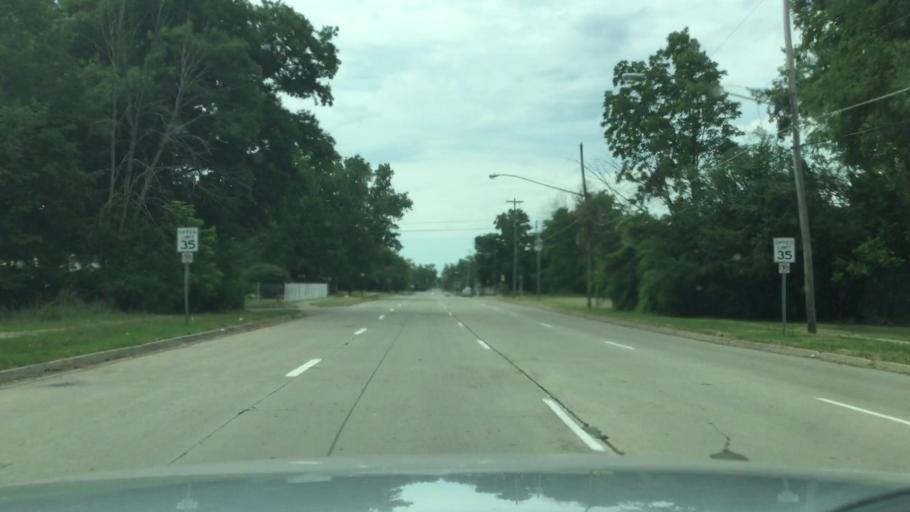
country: US
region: Michigan
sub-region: Genesee County
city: Beecher
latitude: 43.0653
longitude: -83.6845
